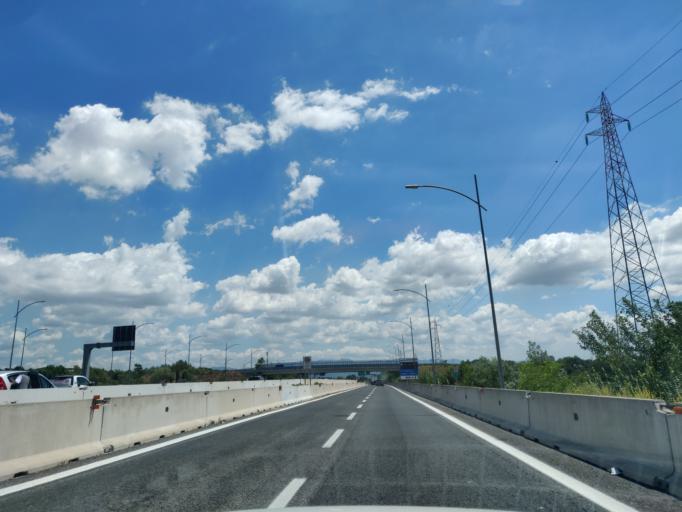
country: IT
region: Latium
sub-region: Citta metropolitana di Roma Capitale
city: Setteville
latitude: 41.9232
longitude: 12.6268
